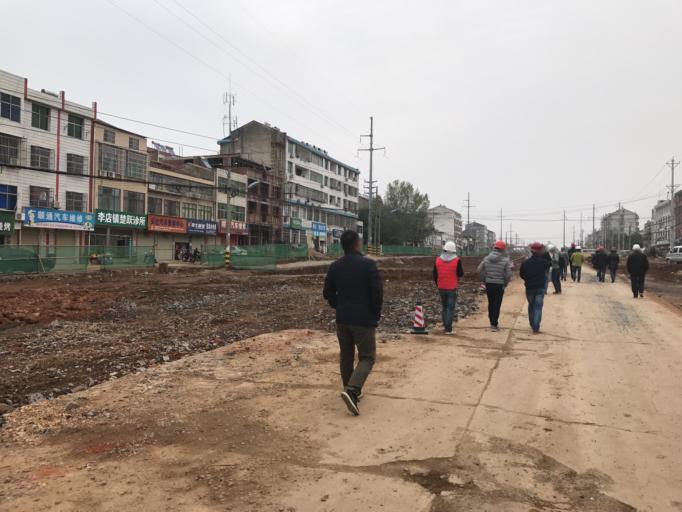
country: CN
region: Hubei
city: Anlu
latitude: 31.2523
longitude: 113.7042
